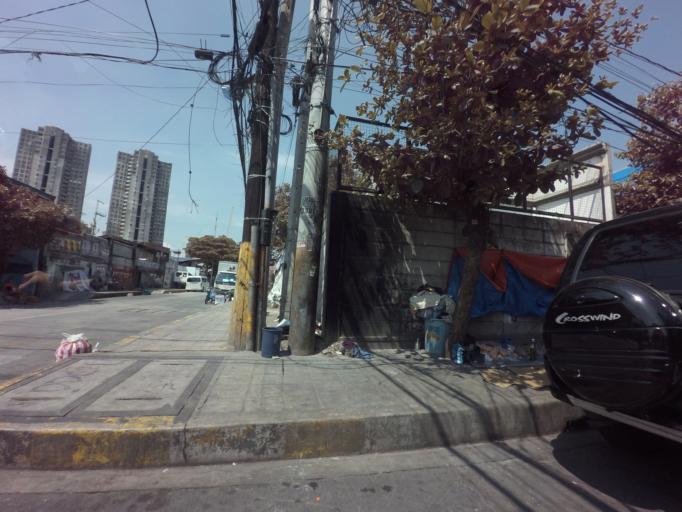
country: PH
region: Metro Manila
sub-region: Makati City
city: Makati City
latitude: 14.5693
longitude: 121.0122
